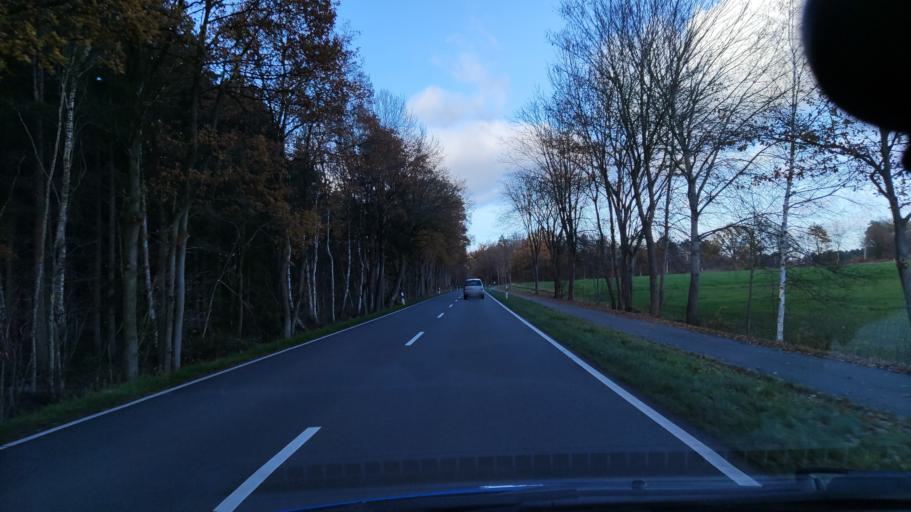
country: DE
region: Lower Saxony
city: Schneverdingen
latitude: 53.0706
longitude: 9.8151
